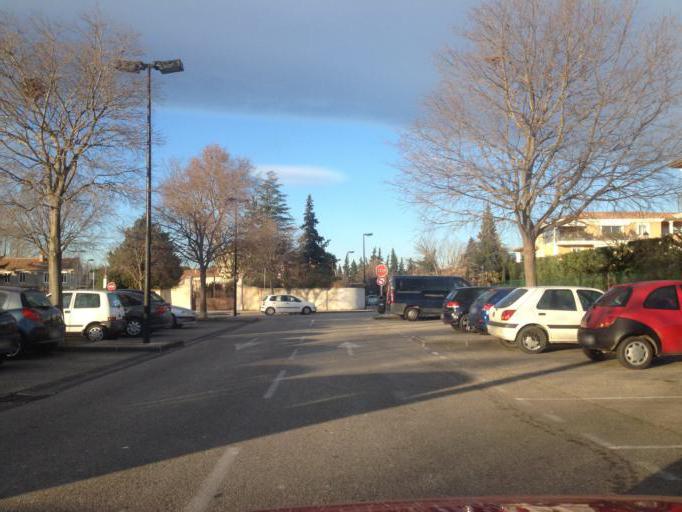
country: FR
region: Provence-Alpes-Cote d'Azur
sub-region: Departement du Vaucluse
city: Orange
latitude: 44.1412
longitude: 4.8084
